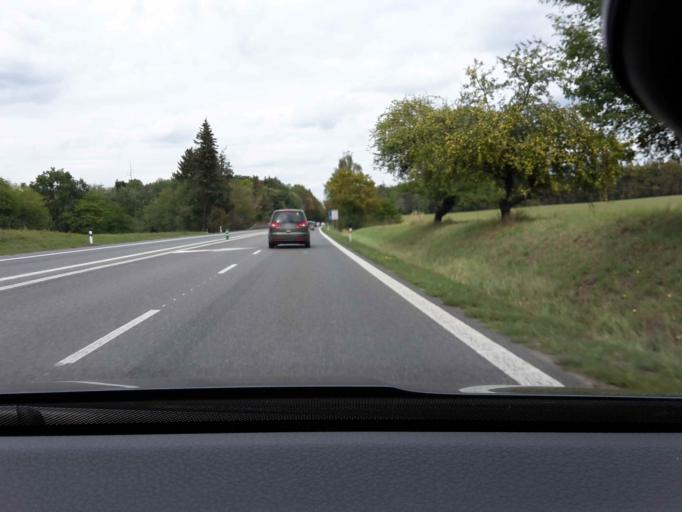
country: CZ
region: Central Bohemia
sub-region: Okres Benesov
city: Benesov
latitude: 49.8042
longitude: 14.6802
